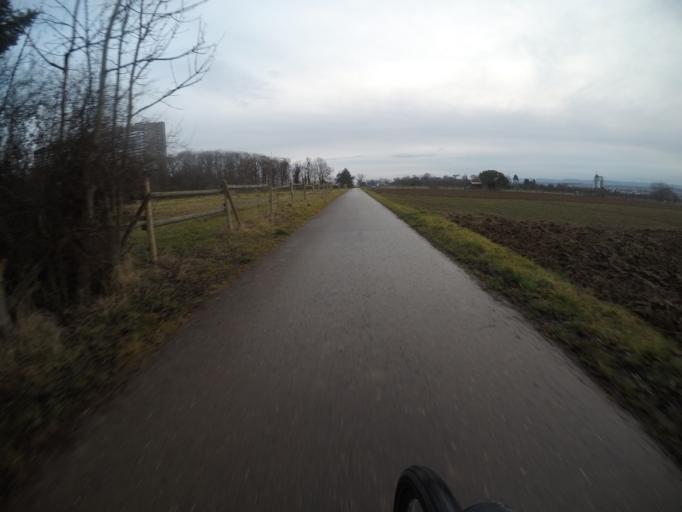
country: DE
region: Baden-Wuerttemberg
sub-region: Regierungsbezirk Stuttgart
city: Leinfelden-Echterdingen
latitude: 48.7218
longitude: 9.1890
